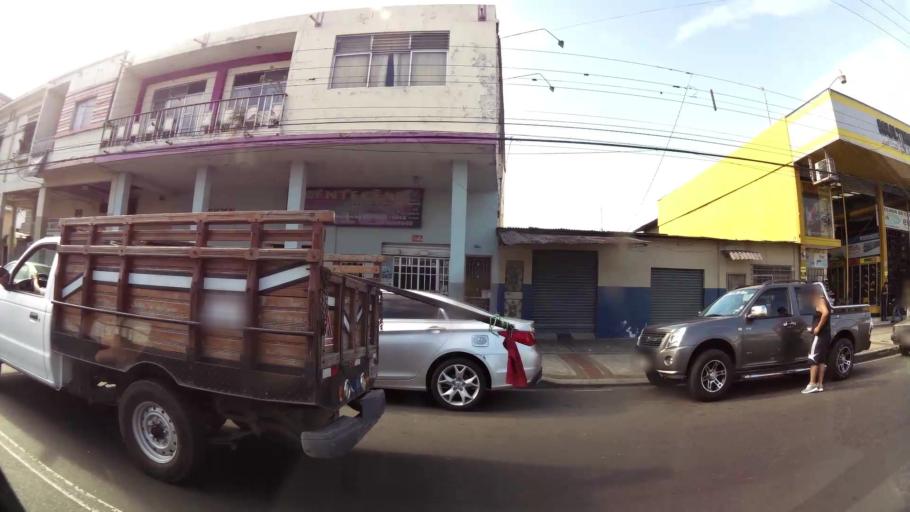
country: EC
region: Guayas
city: Guayaquil
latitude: -2.2023
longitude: -79.9134
